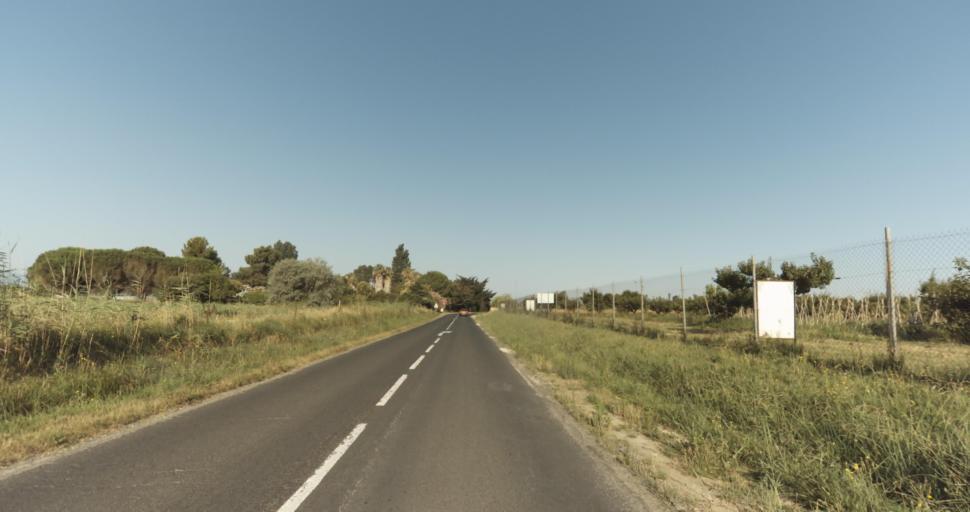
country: FR
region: Languedoc-Roussillon
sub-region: Departement des Pyrenees-Orientales
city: Alenya
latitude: 42.6363
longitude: 2.9992
